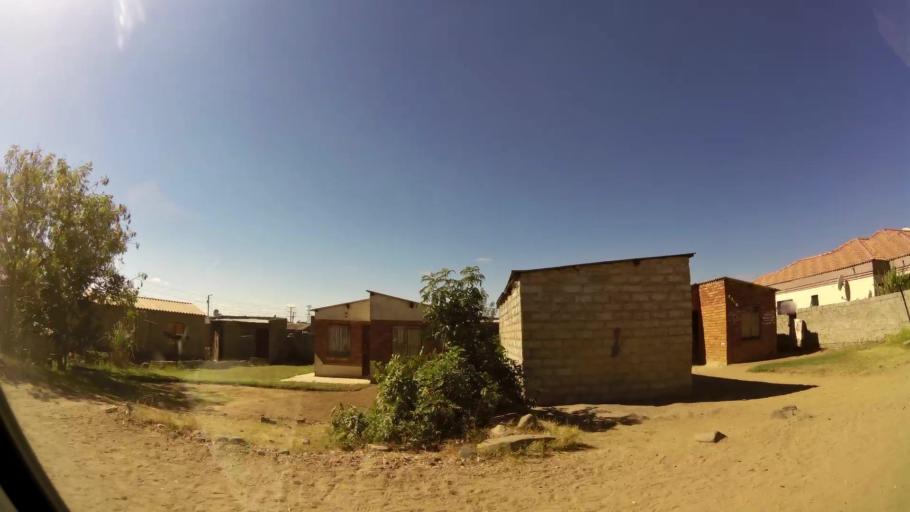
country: ZA
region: Limpopo
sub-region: Capricorn District Municipality
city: Polokwane
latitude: -23.8896
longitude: 29.4178
